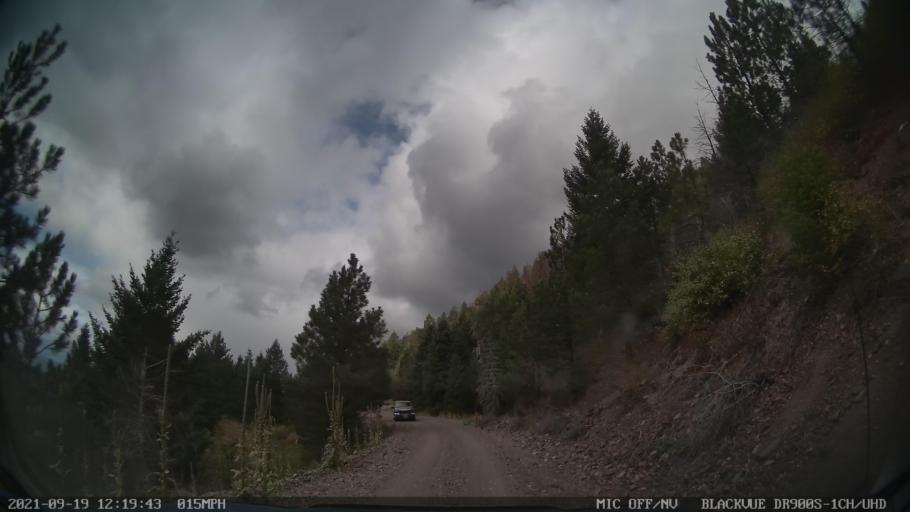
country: US
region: Montana
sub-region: Missoula County
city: Seeley Lake
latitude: 47.1794
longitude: -113.3709
